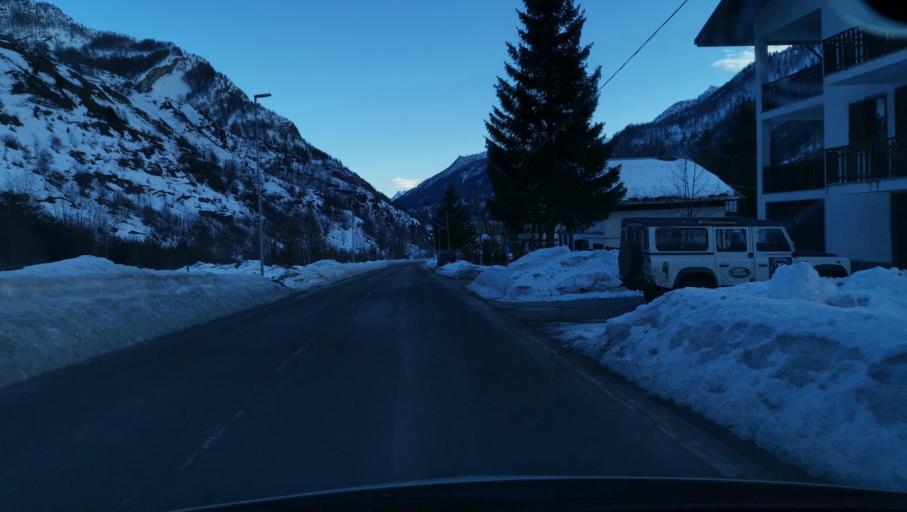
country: IT
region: Piedmont
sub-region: Provincia di Cuneo
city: Bersezio
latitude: 44.3685
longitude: 6.9843
